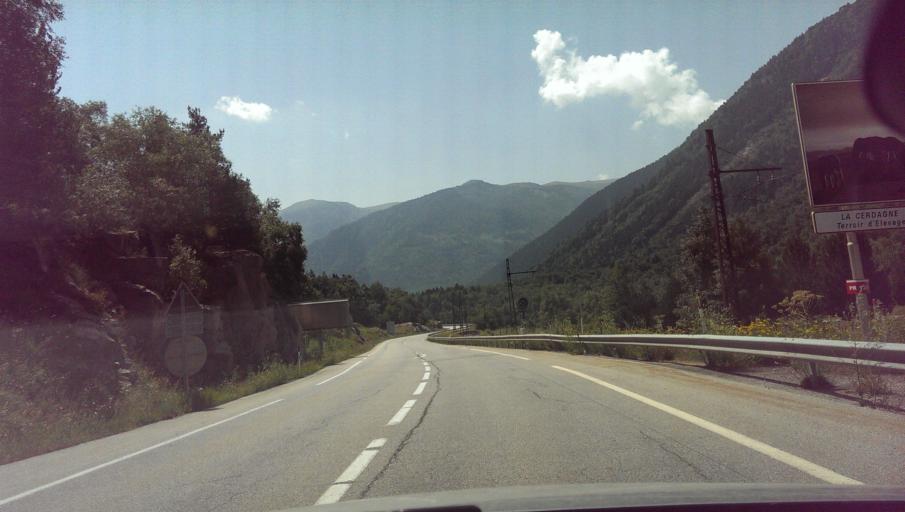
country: AD
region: Encamp
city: Pas de la Casa
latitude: 42.5347
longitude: 1.8227
